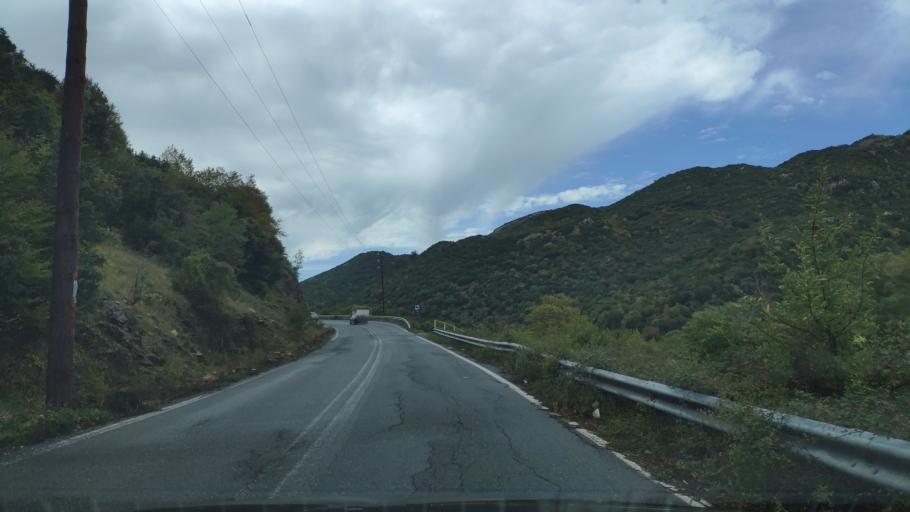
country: GR
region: Peloponnese
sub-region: Nomos Arkadias
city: Dimitsana
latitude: 37.6121
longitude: 22.0429
